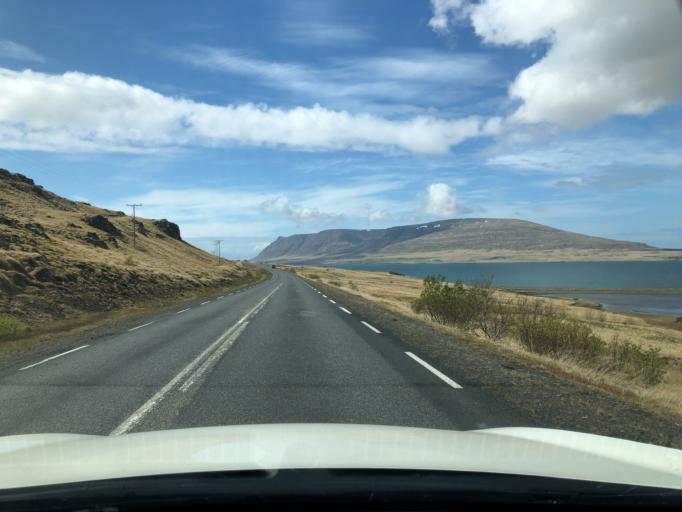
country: IS
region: Capital Region
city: Mosfellsbaer
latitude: 64.3328
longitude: -21.7242
